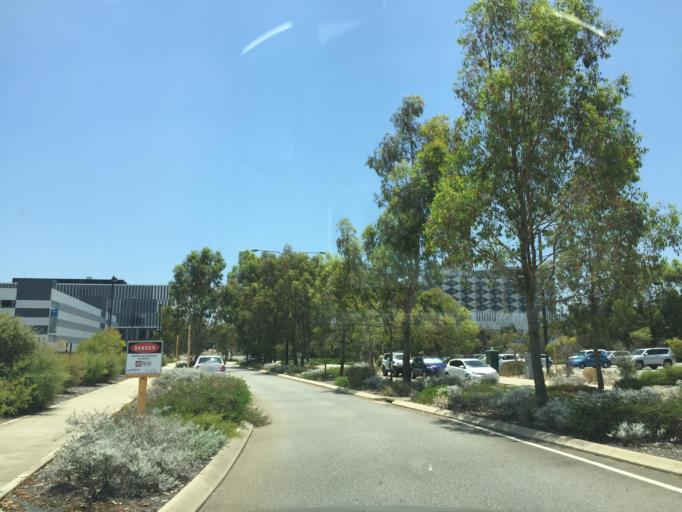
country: AU
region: Western Australia
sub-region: Melville
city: Winthrop
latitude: -32.0732
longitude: 115.8449
